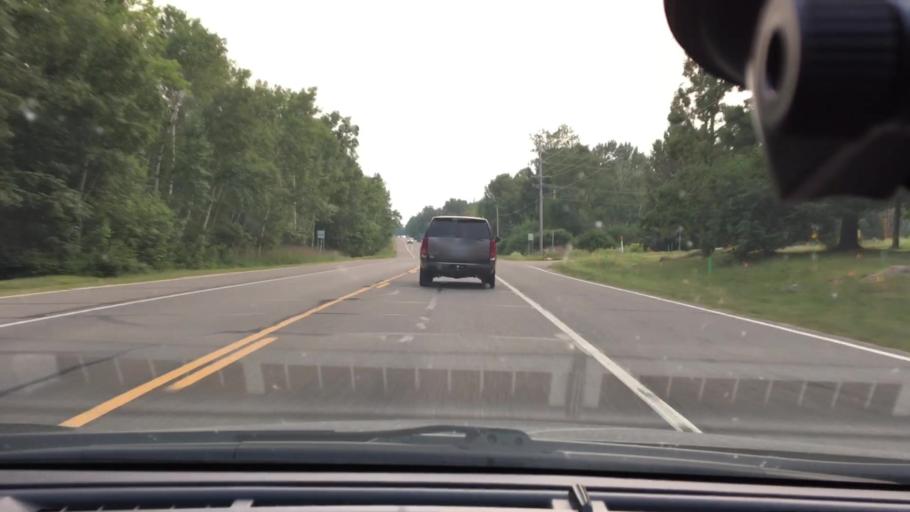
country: US
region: Minnesota
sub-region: Crow Wing County
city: Crosby
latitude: 46.4901
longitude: -93.9267
